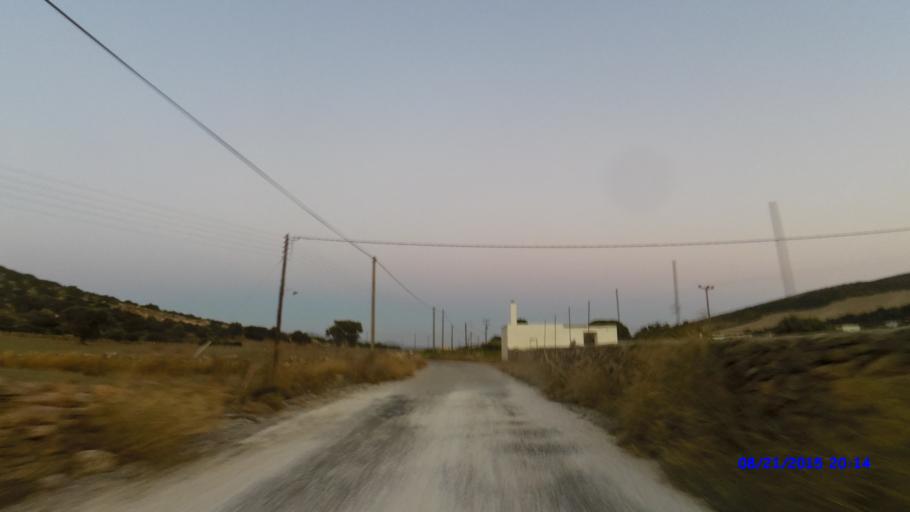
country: GR
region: South Aegean
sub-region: Nomos Kykladon
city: Antiparos
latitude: 37.0098
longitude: 25.0656
